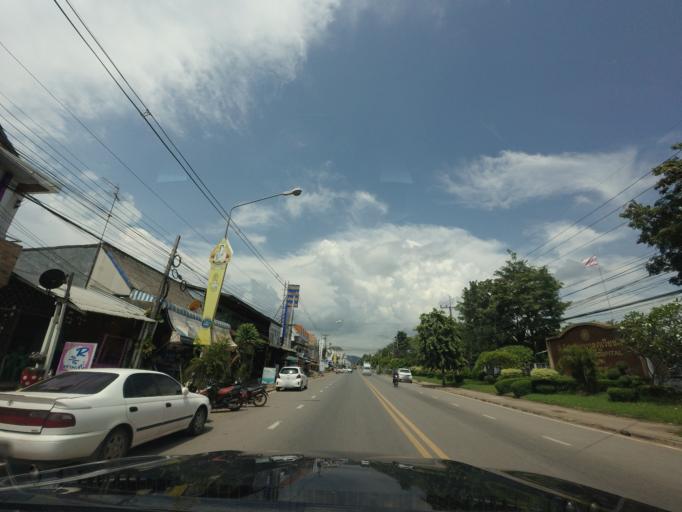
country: TH
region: Khon Kaen
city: Phu Wiang
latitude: 16.6515
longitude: 102.3796
